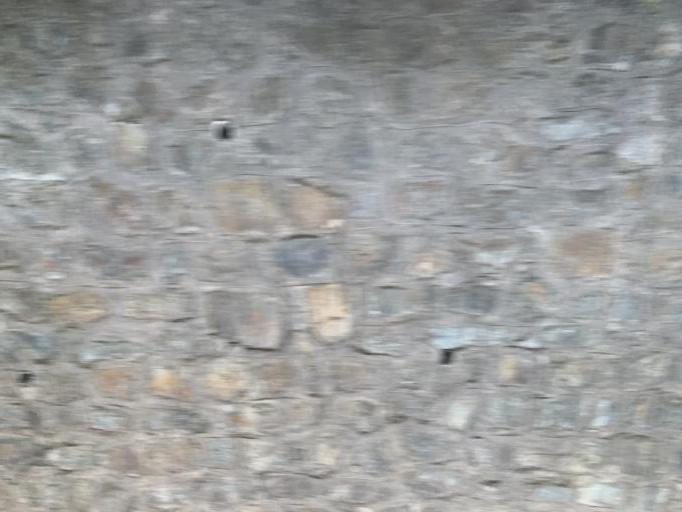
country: TR
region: Trabzon
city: Dernekpazari
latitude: 40.8576
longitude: 40.2795
